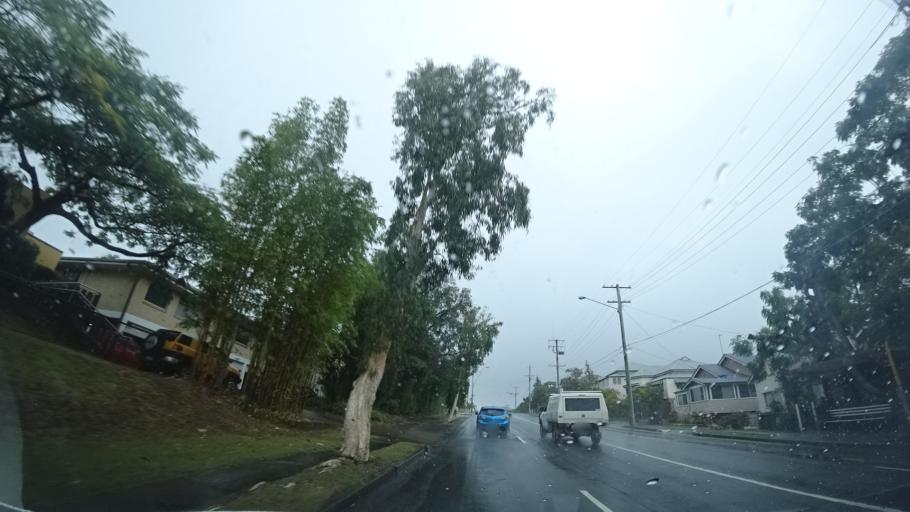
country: AU
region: Queensland
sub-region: Brisbane
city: Toowong
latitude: -27.4768
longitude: 152.9919
